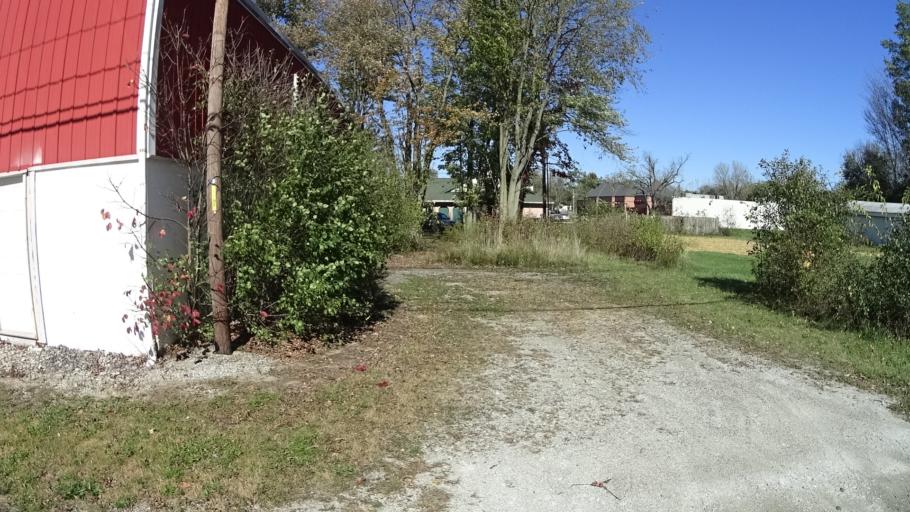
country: US
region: Ohio
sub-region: Lorain County
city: Oberlin
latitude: 41.2824
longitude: -82.2170
